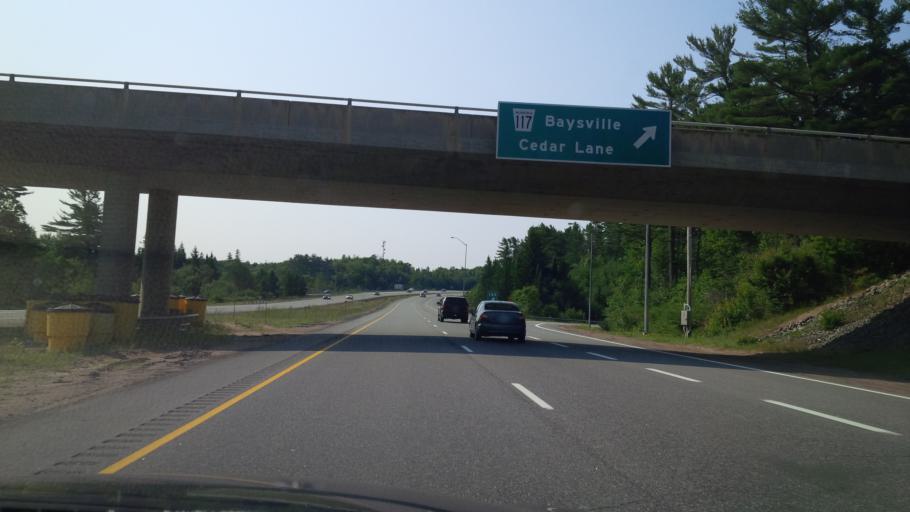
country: CA
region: Ontario
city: Bracebridge
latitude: 45.0864
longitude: -79.2987
